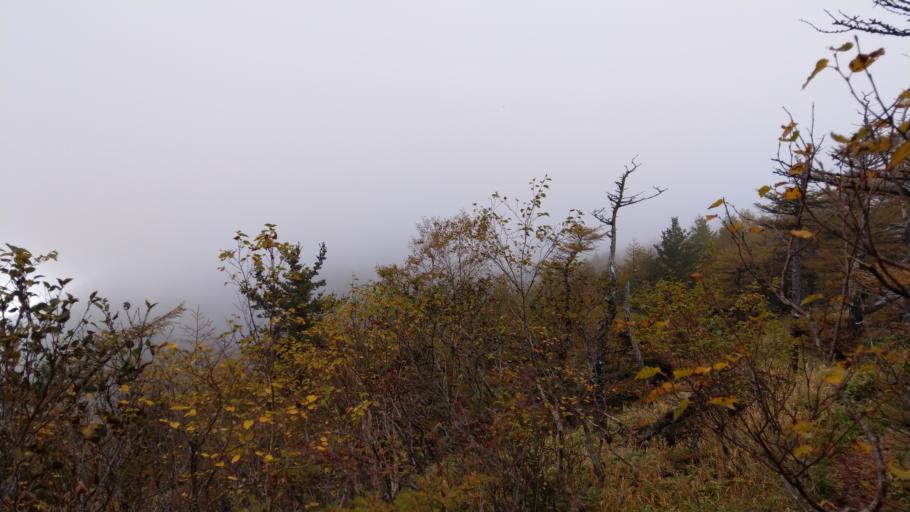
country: JP
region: Nagano
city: Komoro
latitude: 36.4042
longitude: 138.4650
